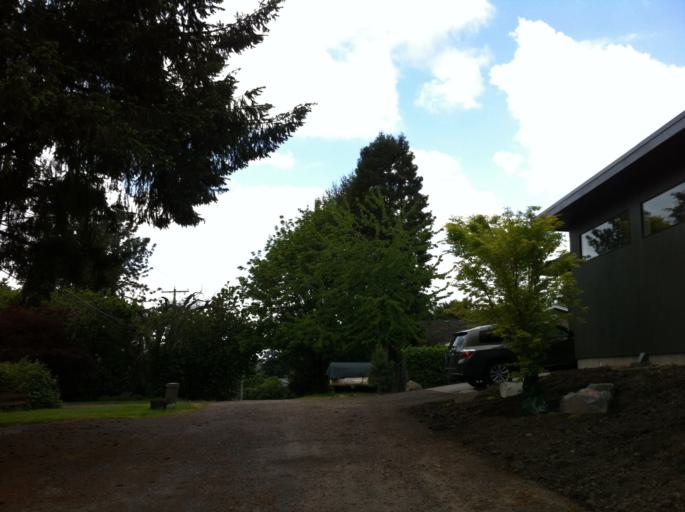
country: US
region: Oregon
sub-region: Clackamas County
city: Lake Oswego
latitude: 45.4643
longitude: -122.6857
